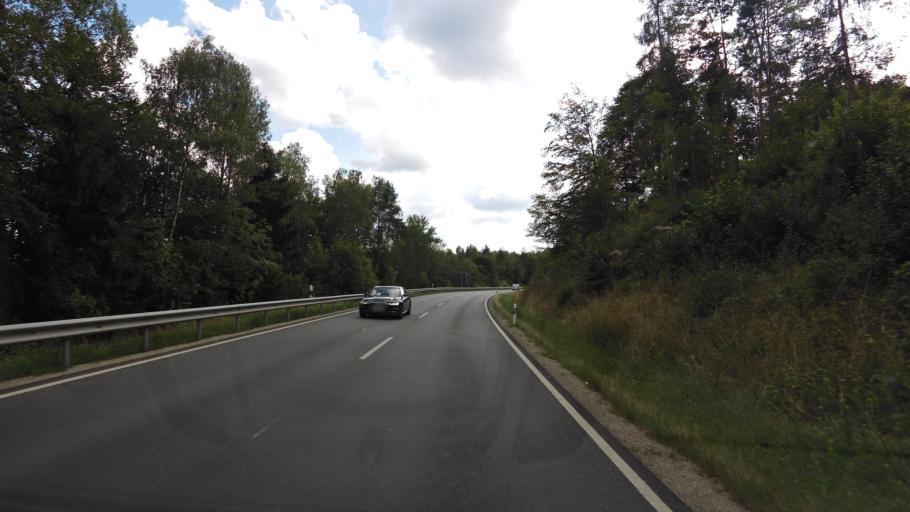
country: DE
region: Bavaria
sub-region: Lower Bavaria
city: Loitzendorf
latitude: 49.1054
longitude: 12.6508
